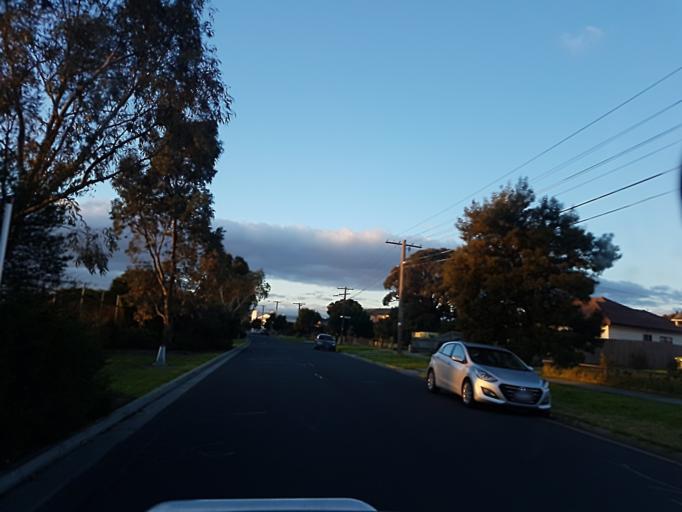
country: AU
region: Victoria
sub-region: Hume
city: Broadmeadows
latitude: -37.6819
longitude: 144.9211
